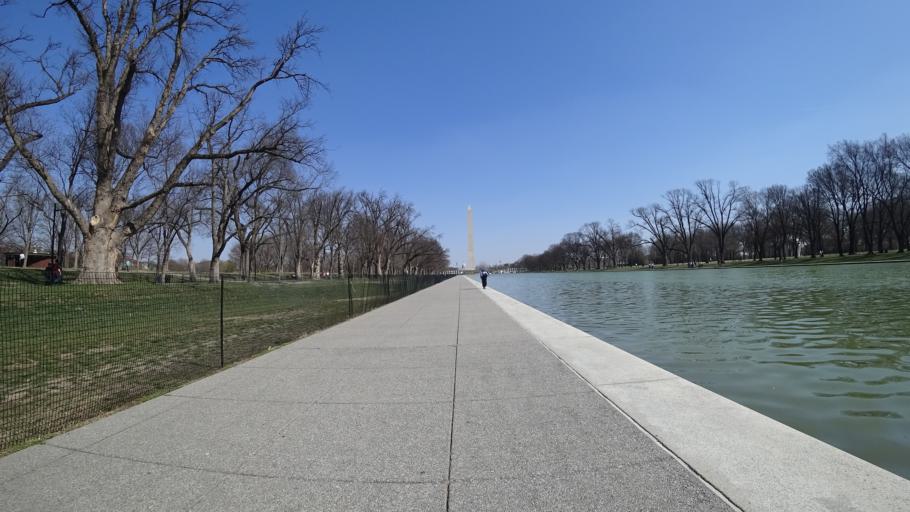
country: US
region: Washington, D.C.
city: Washington, D.C.
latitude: 38.8896
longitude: -77.0460
